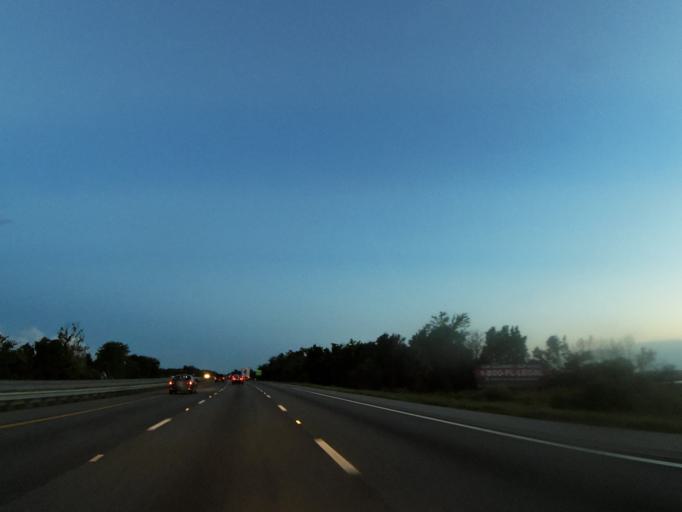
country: US
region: Florida
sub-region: Nassau County
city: Yulee
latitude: 30.5789
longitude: -81.6476
